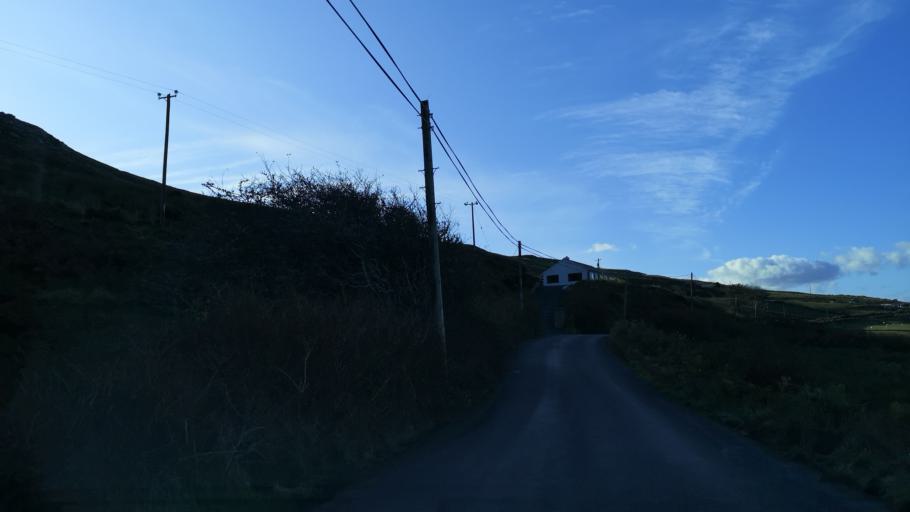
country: IE
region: Connaught
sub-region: County Galway
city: Clifden
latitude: 53.5060
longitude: -10.0828
